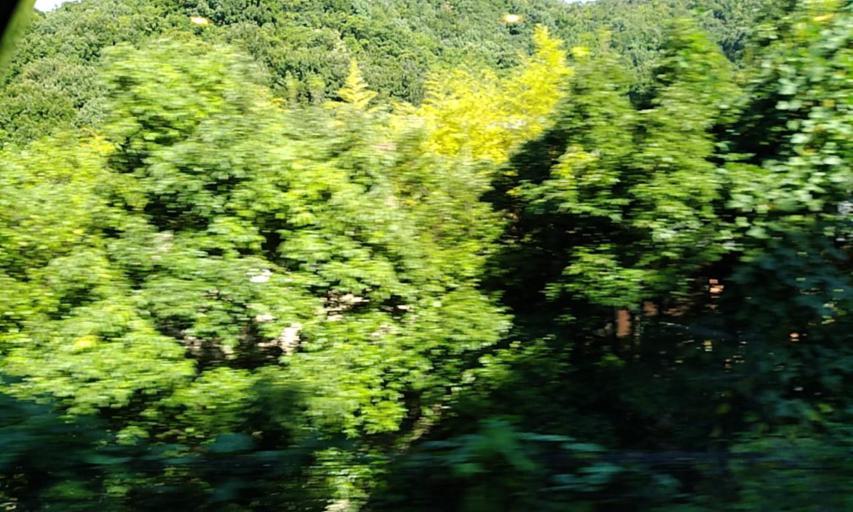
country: JP
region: Kyoto
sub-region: Kyoto-shi
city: Kamigyo-ku
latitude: 35.0638
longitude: 135.8045
